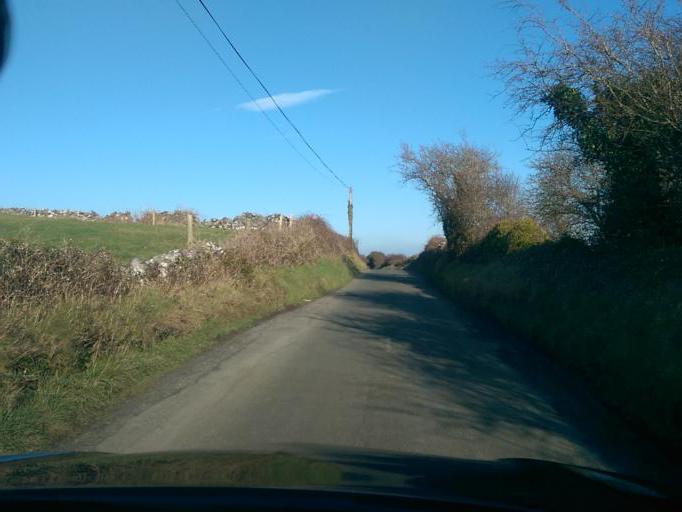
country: IE
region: Connaught
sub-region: County Galway
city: Oranmore
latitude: 53.2114
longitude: -8.8865
